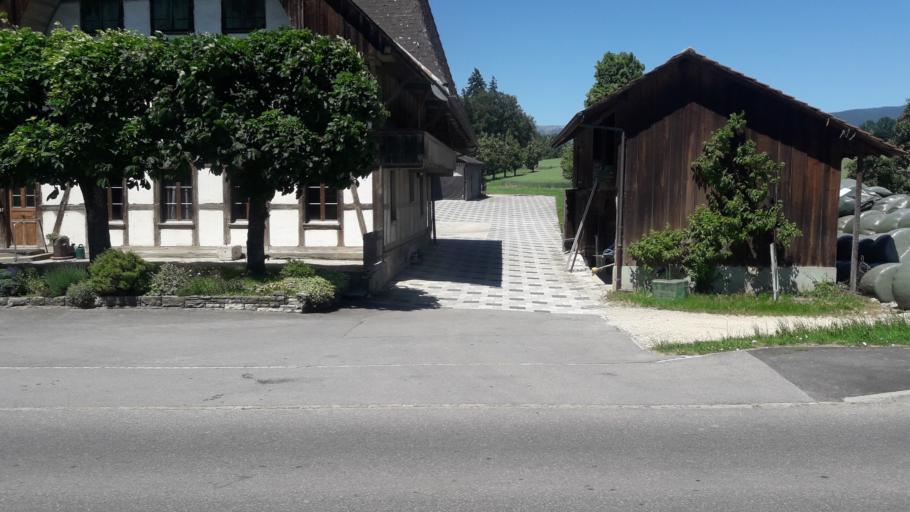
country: CH
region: Bern
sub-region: Seeland District
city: Tauffelen
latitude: 47.0579
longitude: 7.1875
